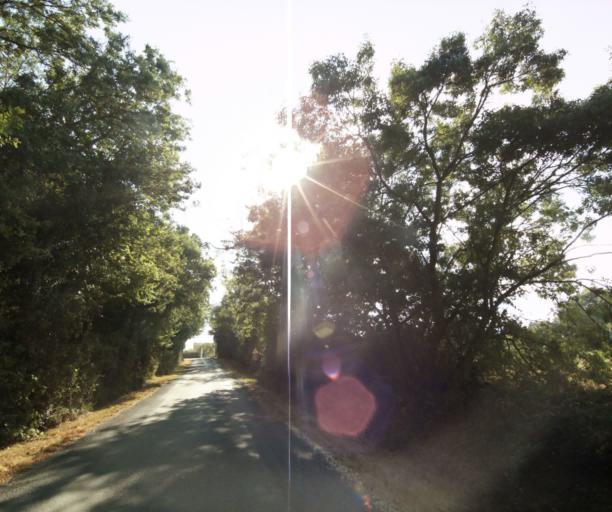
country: FR
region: Poitou-Charentes
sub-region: Departement de la Charente-Maritime
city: Tonnay-Charente
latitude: 45.9633
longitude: -0.8834
